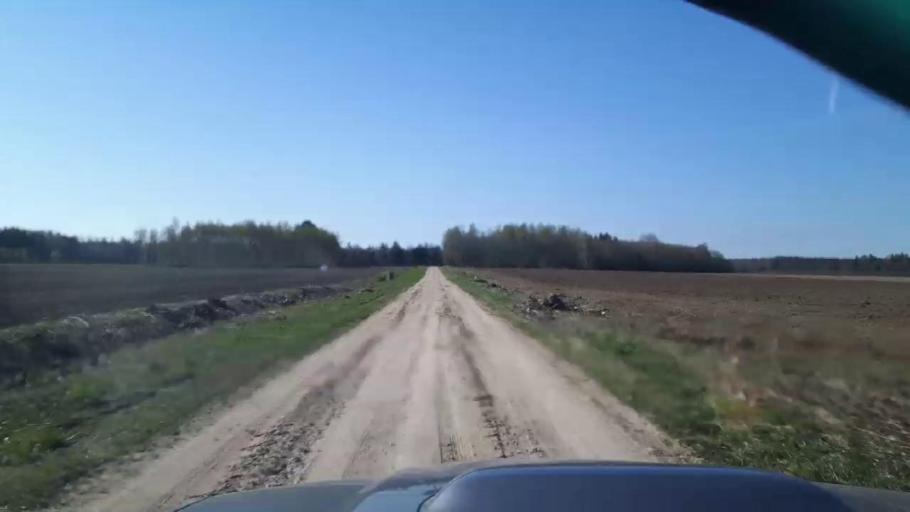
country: EE
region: Paernumaa
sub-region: Tootsi vald
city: Tootsi
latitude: 58.5215
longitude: 24.9293
